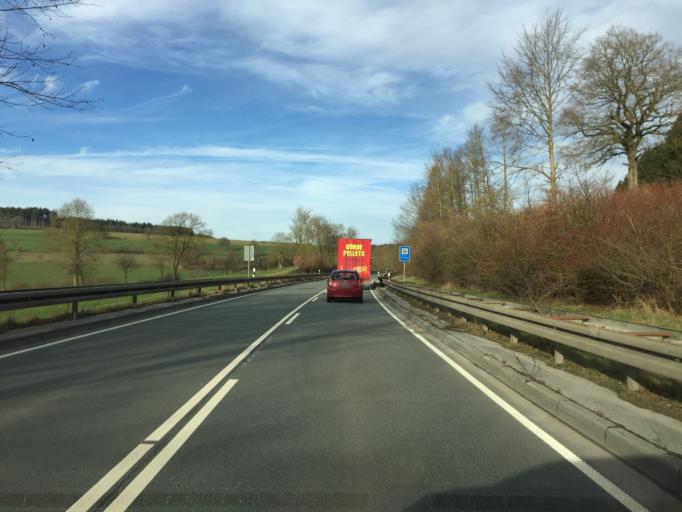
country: DE
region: North Rhine-Westphalia
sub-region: Regierungsbezirk Arnsberg
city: Ruthen
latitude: 51.4583
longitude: 8.4338
